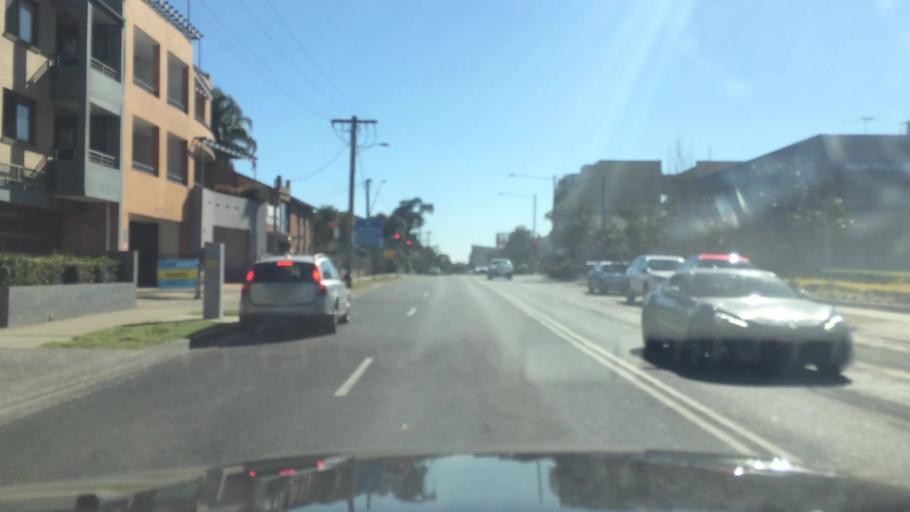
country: AU
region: New South Wales
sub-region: Fairfield
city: Liverpool
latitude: -33.9230
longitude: 150.9212
